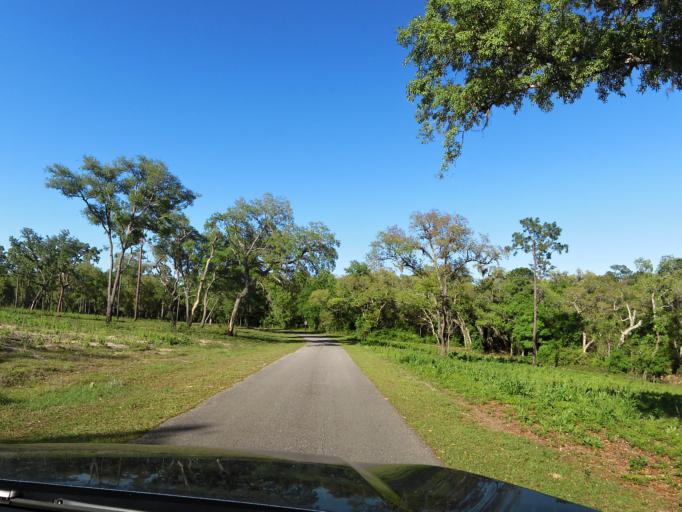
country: US
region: Florida
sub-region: Clay County
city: Keystone Heights
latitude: 29.8280
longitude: -81.9479
